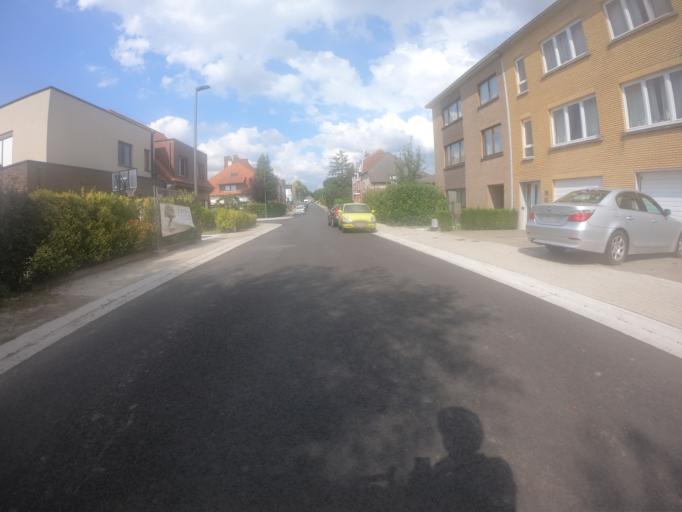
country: BE
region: Flanders
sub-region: Provincie Vlaams-Brabant
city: Dilbeek
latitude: 50.8391
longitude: 4.2621
